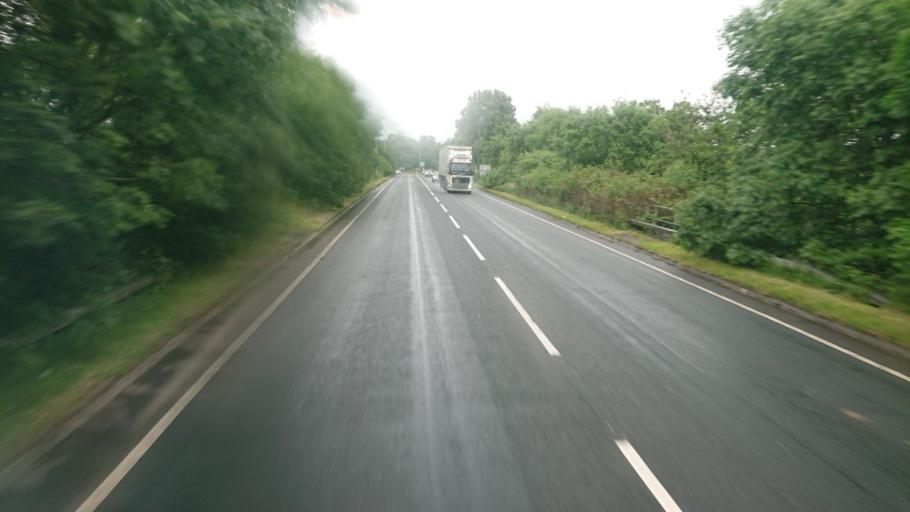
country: GB
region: England
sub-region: Lancashire
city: Morecambe
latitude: 54.0418
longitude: -2.8584
